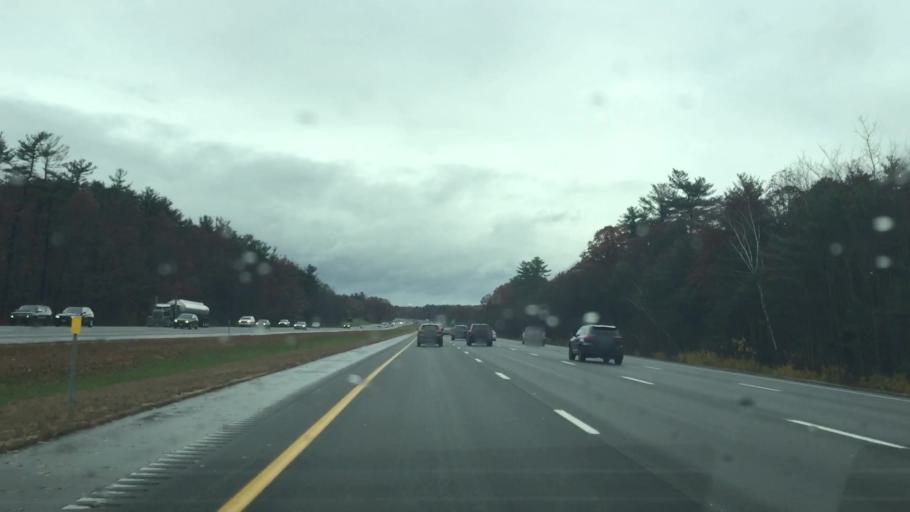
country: US
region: New Hampshire
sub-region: Rockingham County
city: Hampton Falls
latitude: 42.9234
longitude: -70.8680
